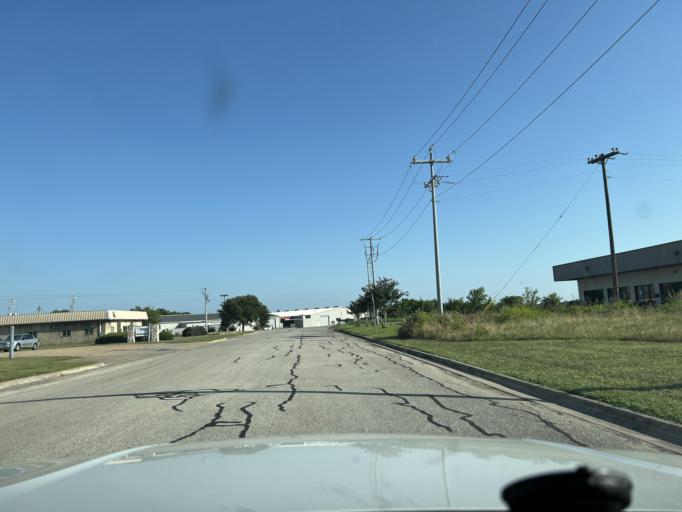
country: US
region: Texas
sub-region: Washington County
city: Brenham
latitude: 30.1420
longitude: -96.3688
